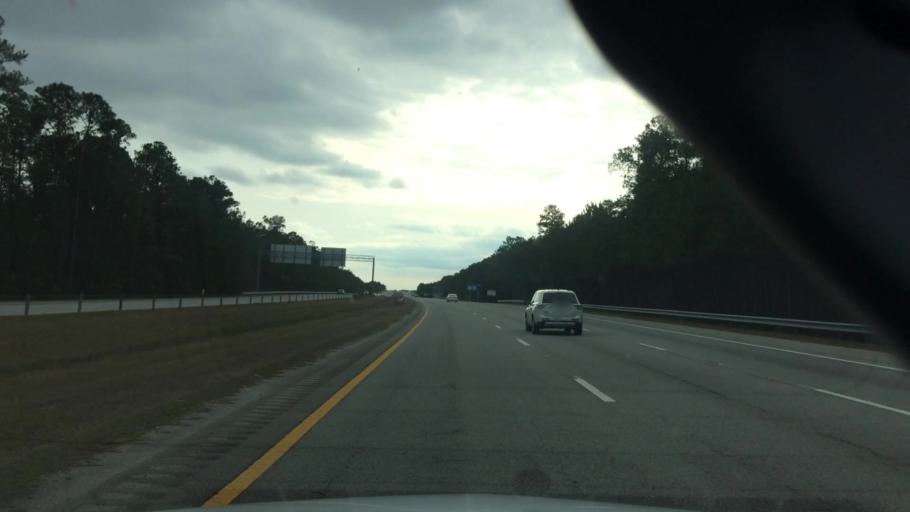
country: US
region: South Carolina
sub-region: Horry County
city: North Myrtle Beach
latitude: 33.8630
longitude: -78.6949
